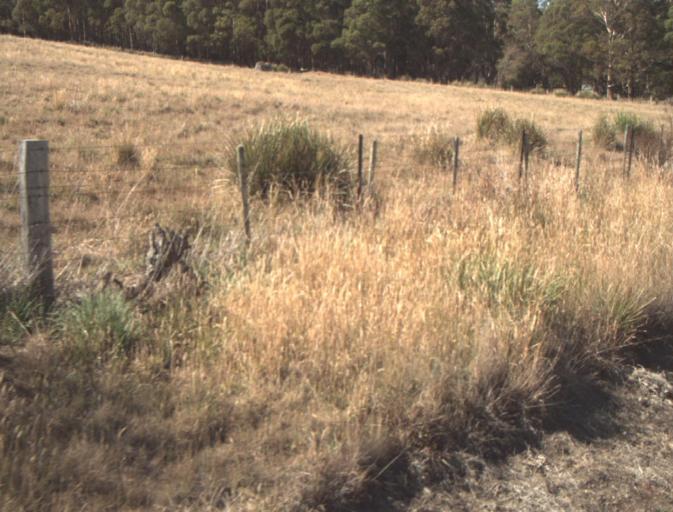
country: AU
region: Tasmania
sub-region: Launceston
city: Newstead
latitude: -41.3131
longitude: 147.3210
